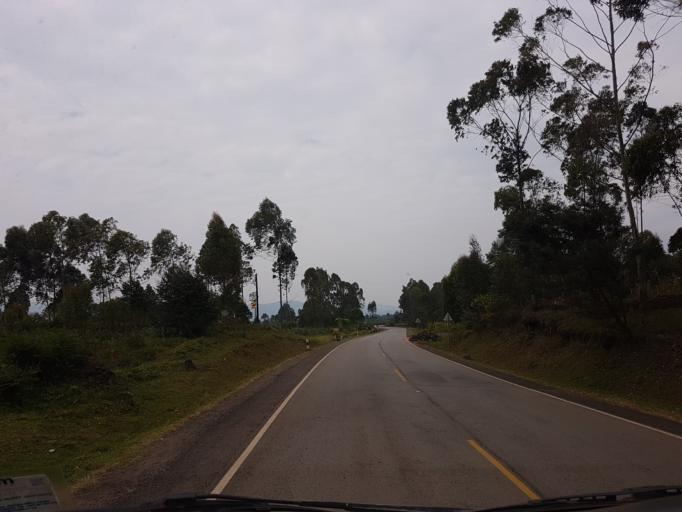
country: UG
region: Western Region
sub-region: Kisoro District
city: Kisoro
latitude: -1.3146
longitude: 29.7234
